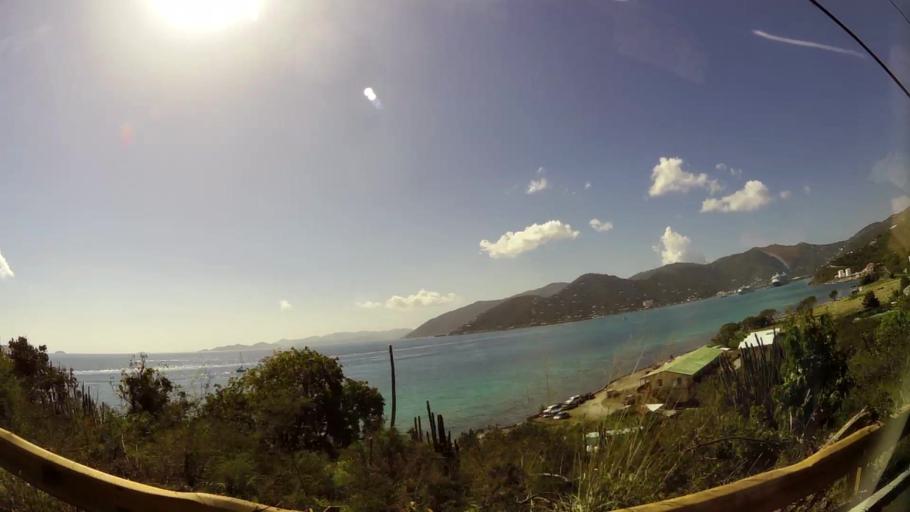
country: VG
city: Tortola
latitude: 18.4141
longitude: -64.5942
